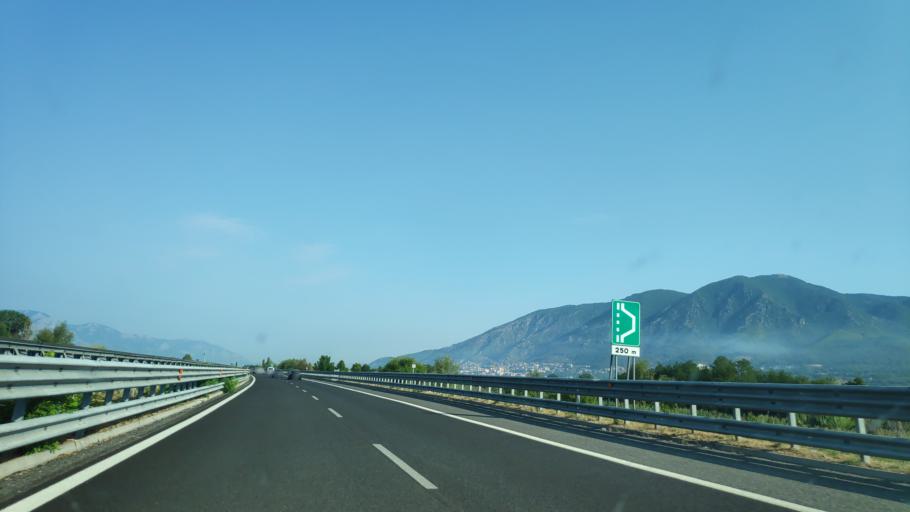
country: IT
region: Campania
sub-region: Provincia di Salerno
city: Sala Consilina
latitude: 40.3605
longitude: 15.6097
